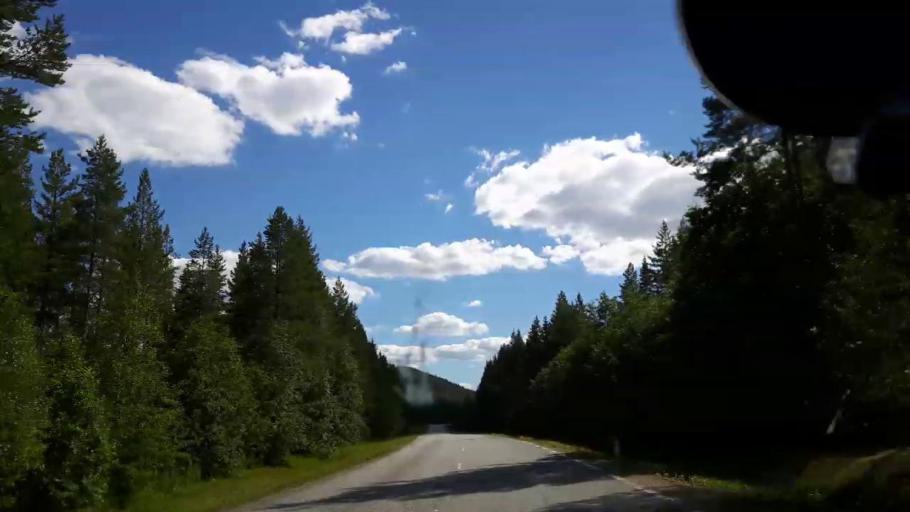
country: SE
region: Jaemtland
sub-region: Ragunda Kommun
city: Hammarstrand
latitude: 62.9530
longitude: 16.2102
